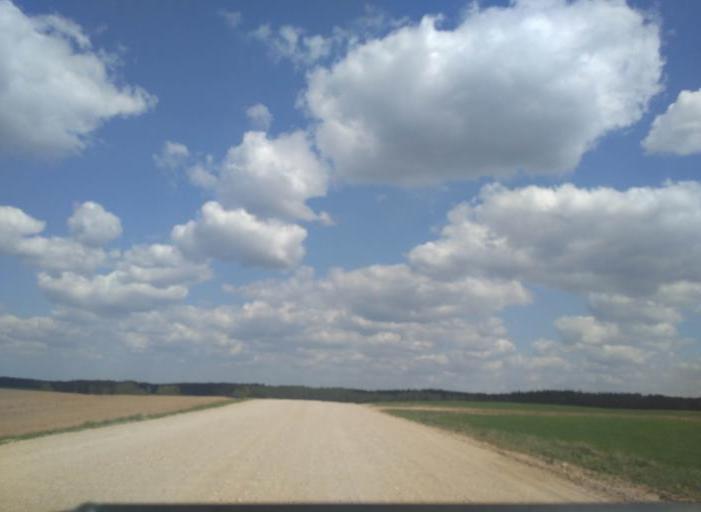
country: BY
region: Minsk
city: Radashkovichy
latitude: 54.2232
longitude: 27.2882
